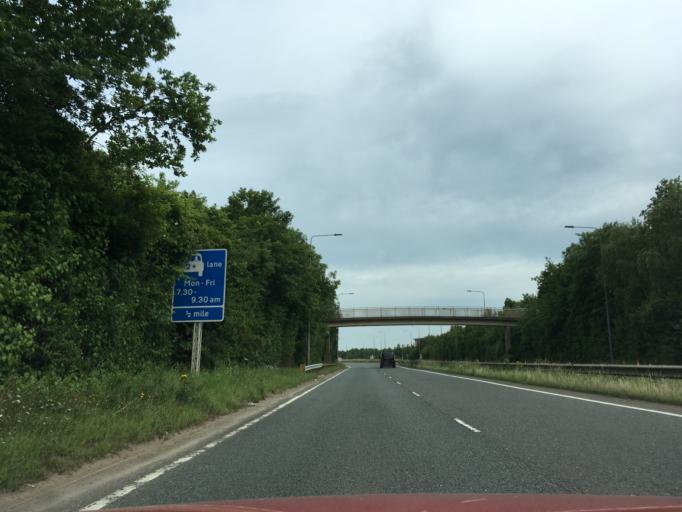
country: GB
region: England
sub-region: South Gloucestershire
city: Mangotsfield
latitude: 51.5024
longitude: -2.4844
